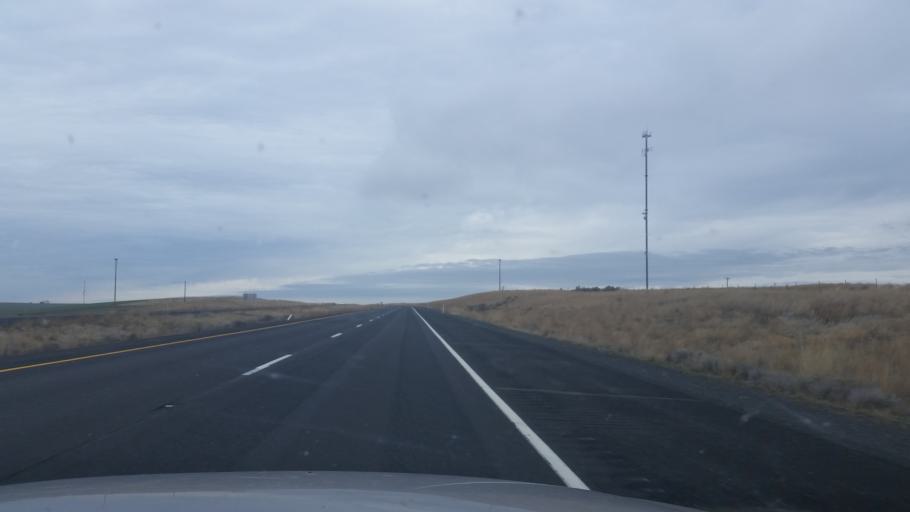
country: US
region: Washington
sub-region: Adams County
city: Ritzville
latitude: 47.1114
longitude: -118.4477
